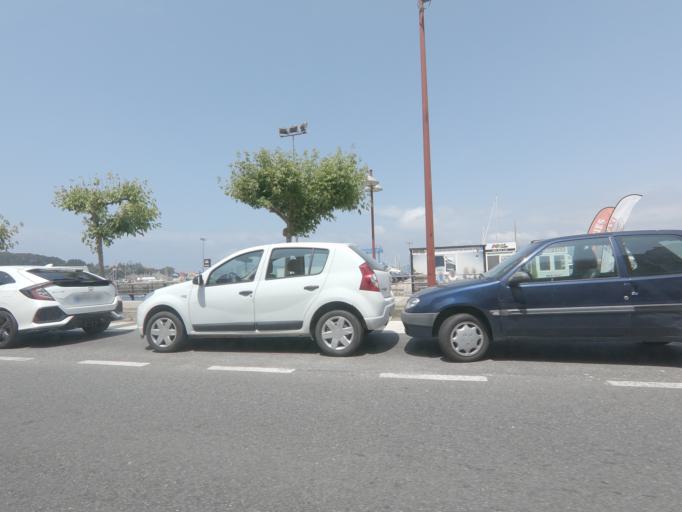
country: ES
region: Galicia
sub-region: Provincia de Pontevedra
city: Baiona
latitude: 42.1177
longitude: -8.8455
